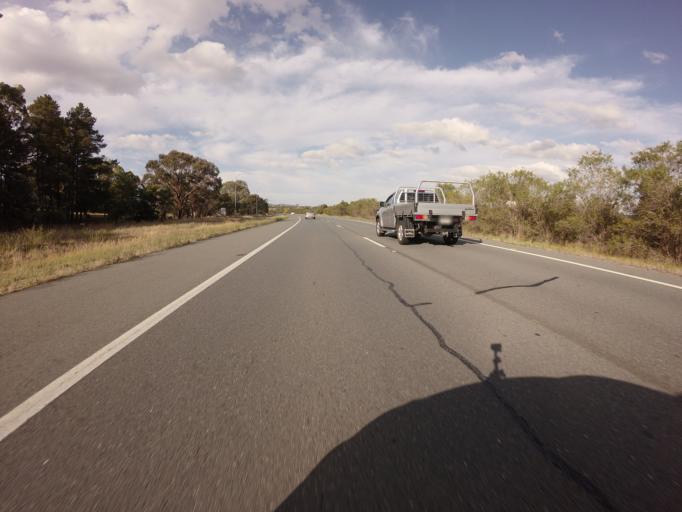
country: AU
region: Australian Capital Territory
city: Kaleen
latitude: -35.2007
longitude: 149.2126
